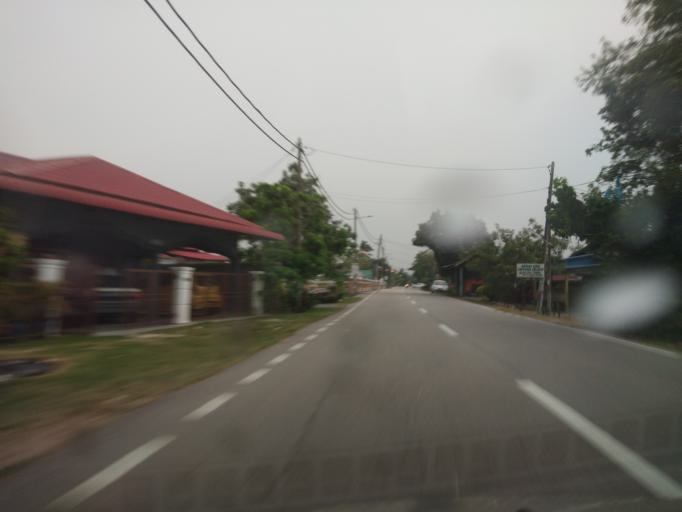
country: MY
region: Penang
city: Permatang Kuching
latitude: 5.4910
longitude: 100.3993
